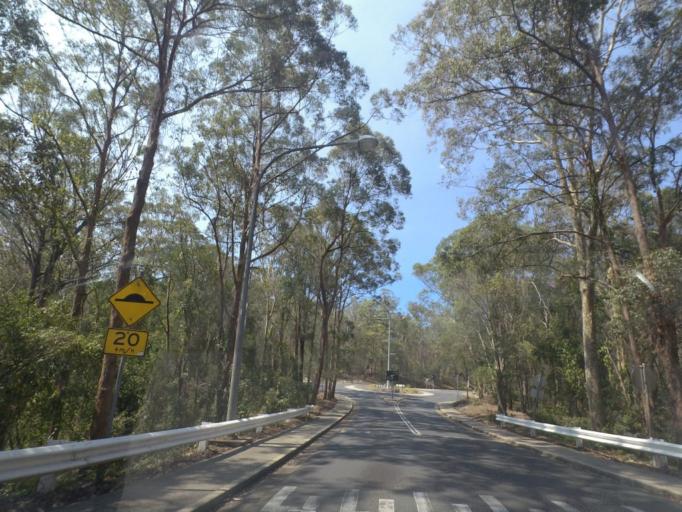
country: AU
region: Queensland
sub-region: Brisbane
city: Nathan
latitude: -27.5513
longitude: 153.0575
